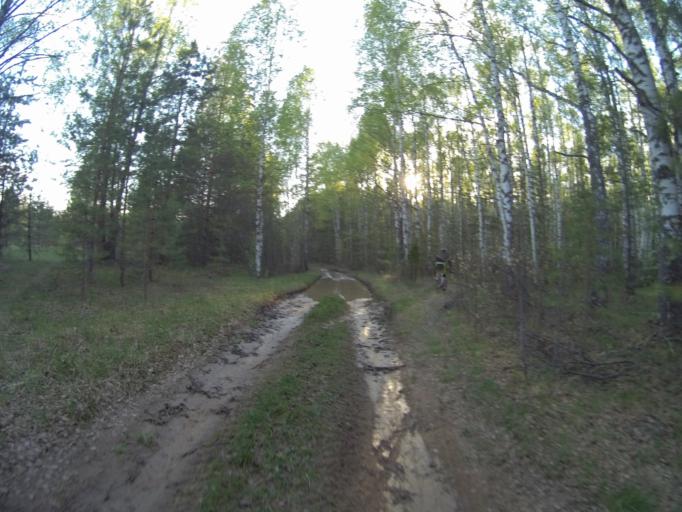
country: RU
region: Vladimir
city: Orgtrud
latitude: 56.0734
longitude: 40.7272
